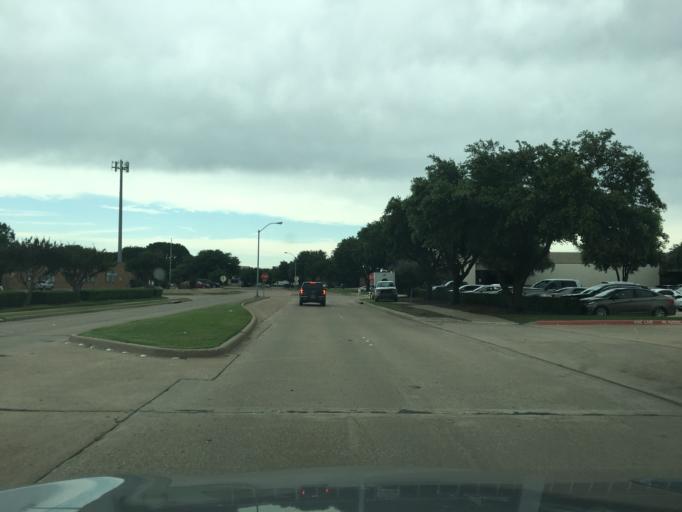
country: US
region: Texas
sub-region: Dallas County
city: Richardson
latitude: 32.9652
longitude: -96.7052
